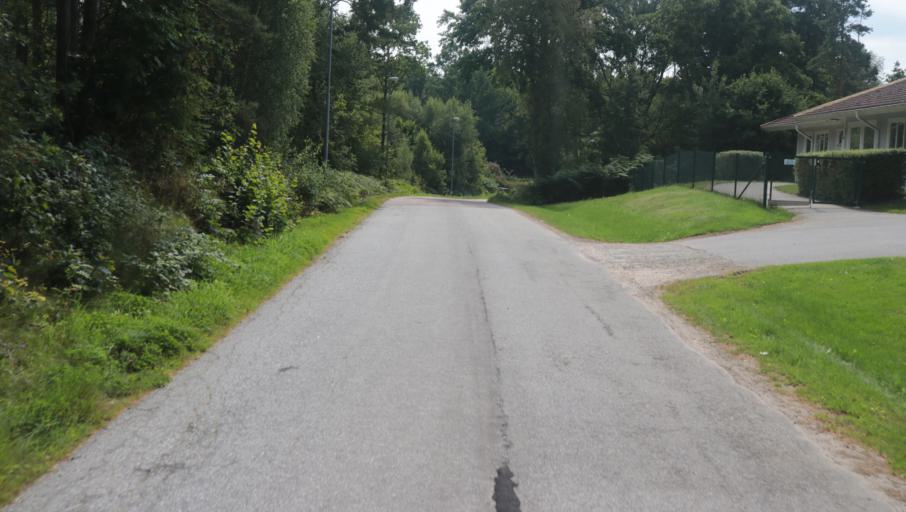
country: SE
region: Blekinge
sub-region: Karlshamns Kommun
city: Morrum
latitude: 56.1888
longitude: 14.7634
